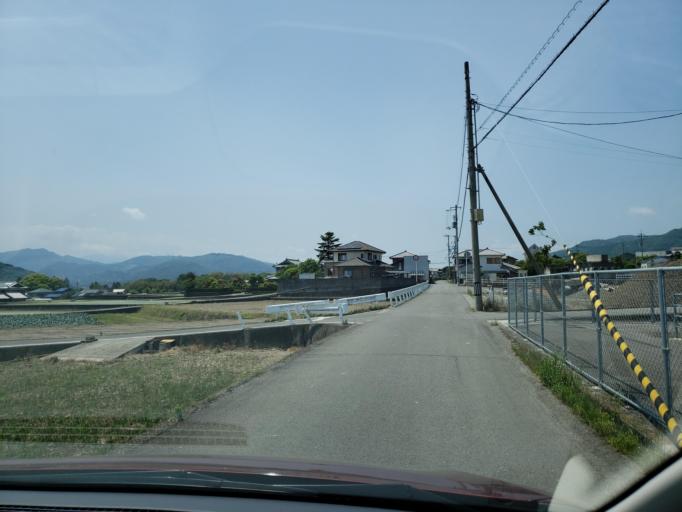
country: JP
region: Tokushima
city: Wakimachi
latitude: 34.0867
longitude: 134.2150
